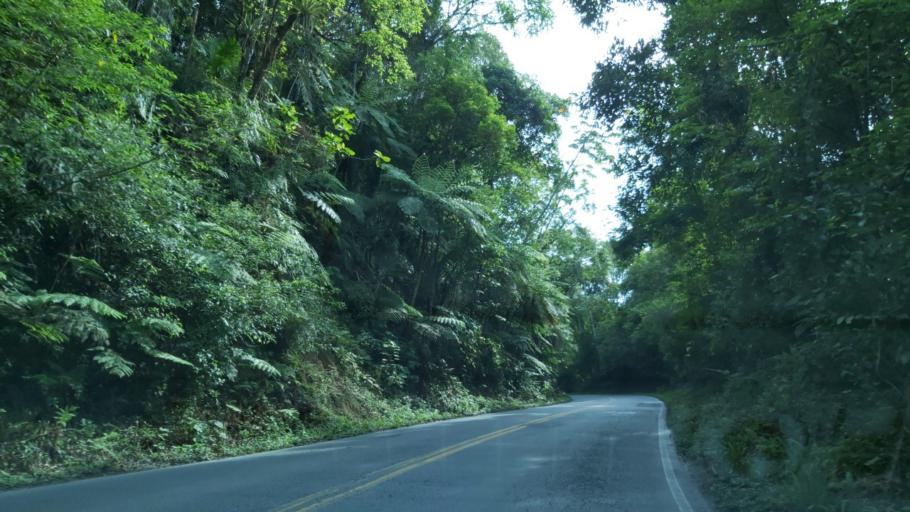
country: BR
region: Sao Paulo
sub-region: Juquia
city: Juquia
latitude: -24.1000
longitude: -47.6253
